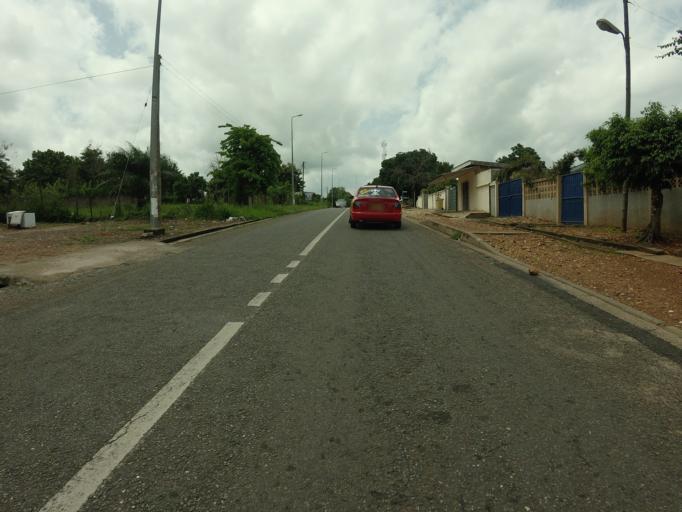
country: GH
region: Volta
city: Ho
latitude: 6.5934
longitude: 0.4733
